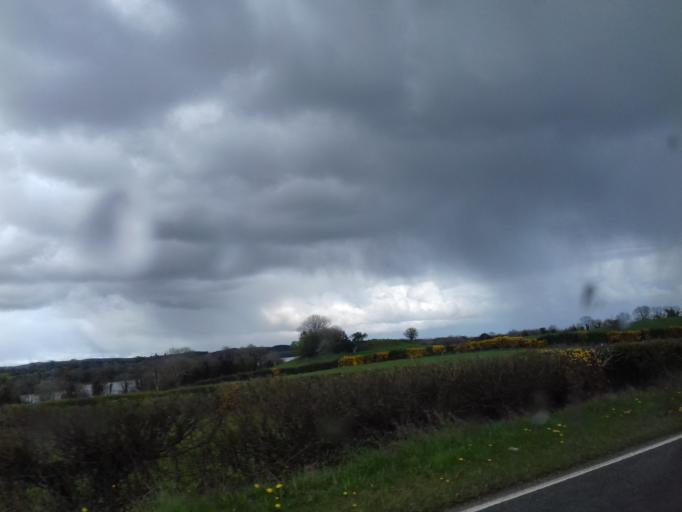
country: IE
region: Ulster
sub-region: County Donegal
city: Ballyshannon
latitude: 54.4696
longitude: -7.9828
